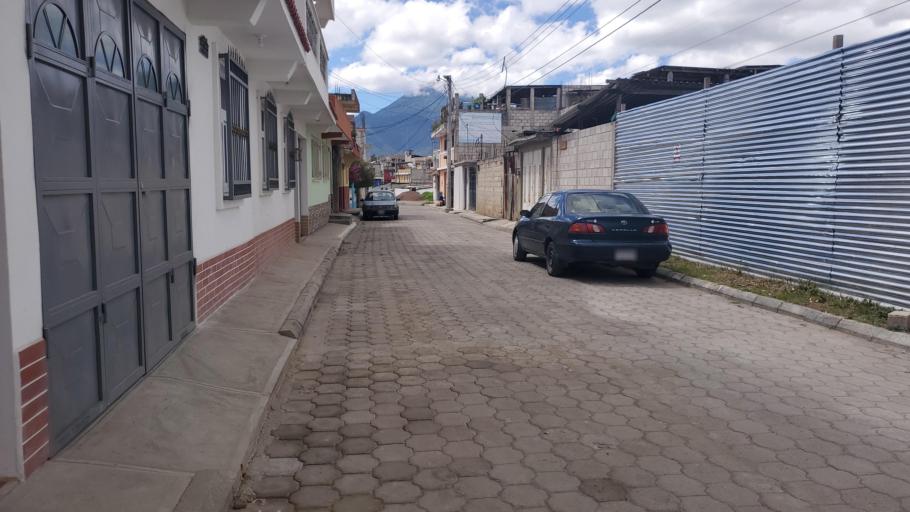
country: GT
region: Quetzaltenango
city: Quetzaltenango
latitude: 14.8366
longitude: -91.5368
